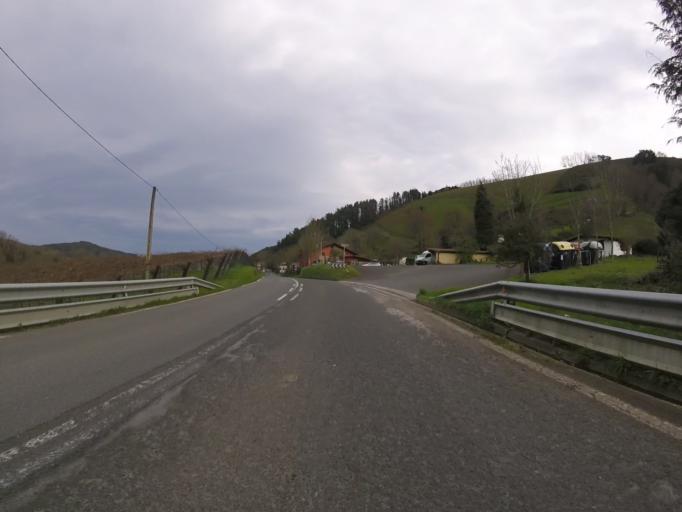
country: ES
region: Basque Country
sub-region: Provincia de Guipuzcoa
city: Aizarnazabal
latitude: 43.2737
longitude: -2.2301
